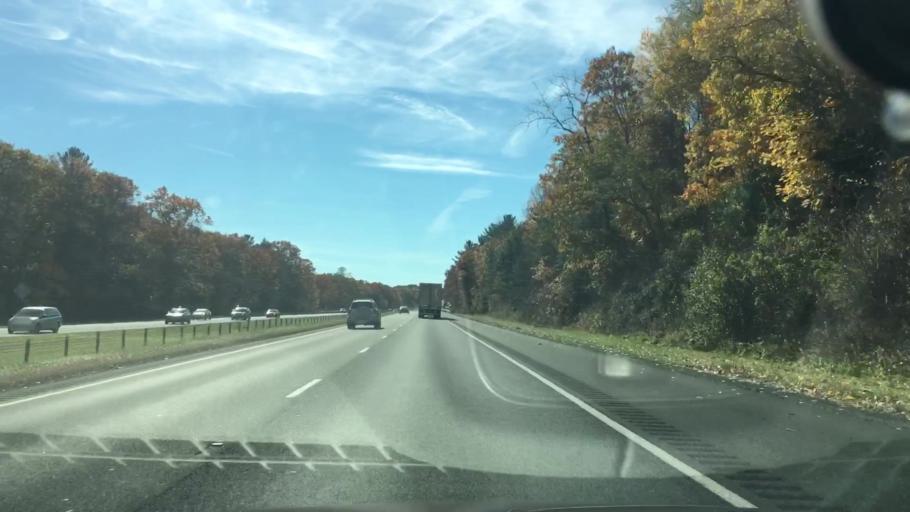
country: US
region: Massachusetts
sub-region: Hampden County
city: Holyoke
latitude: 42.2406
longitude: -72.6302
